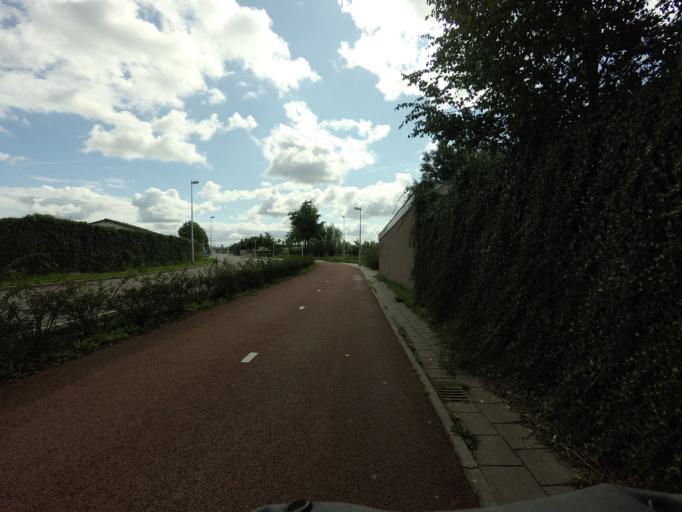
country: NL
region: Utrecht
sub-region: Stichtse Vecht
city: Maarssen
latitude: 52.0811
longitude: 5.0449
